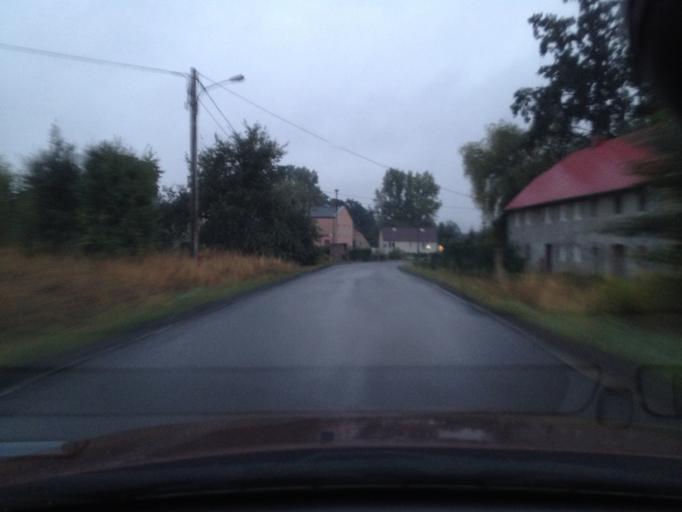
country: PL
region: Lower Silesian Voivodeship
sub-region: Powiat zgorzelecki
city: Piensk
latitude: 51.2102
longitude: 15.0549
